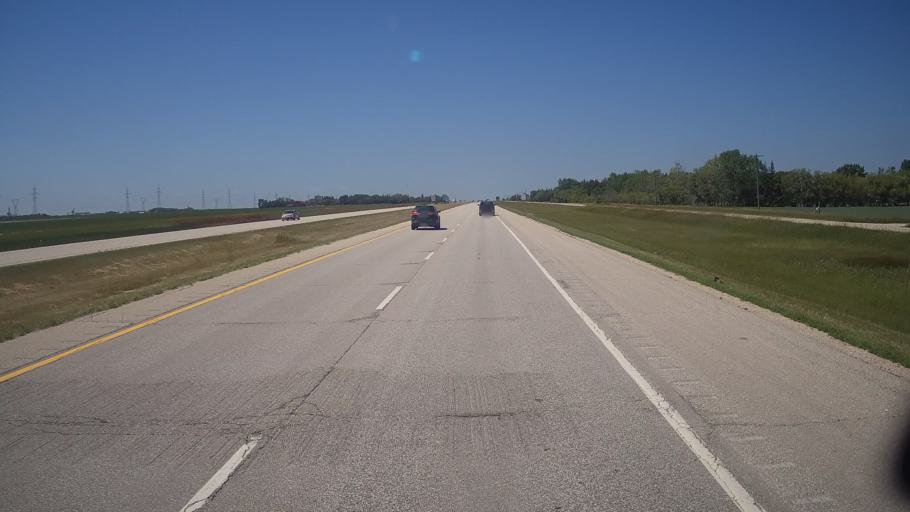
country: CA
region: Manitoba
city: Winnipeg
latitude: 49.9900
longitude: -97.2533
